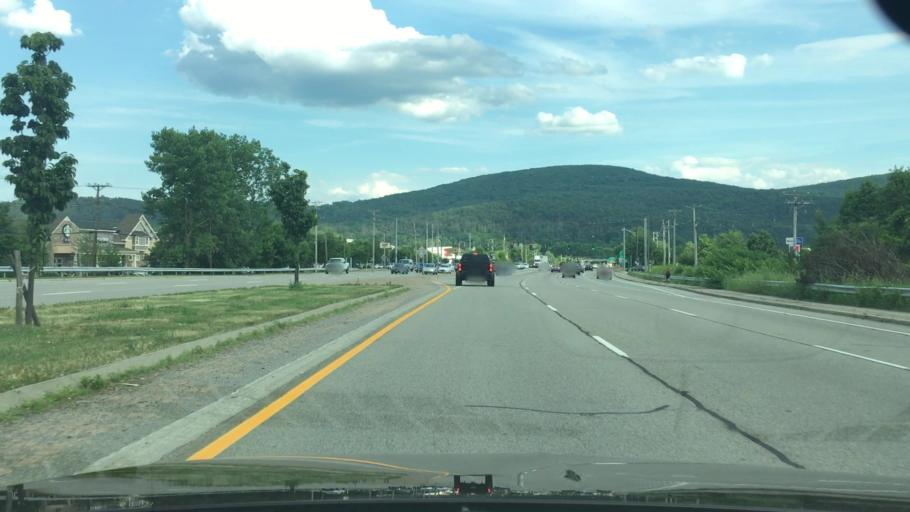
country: US
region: New York
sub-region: Dutchess County
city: Fishkill
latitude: 41.5315
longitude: -73.8949
